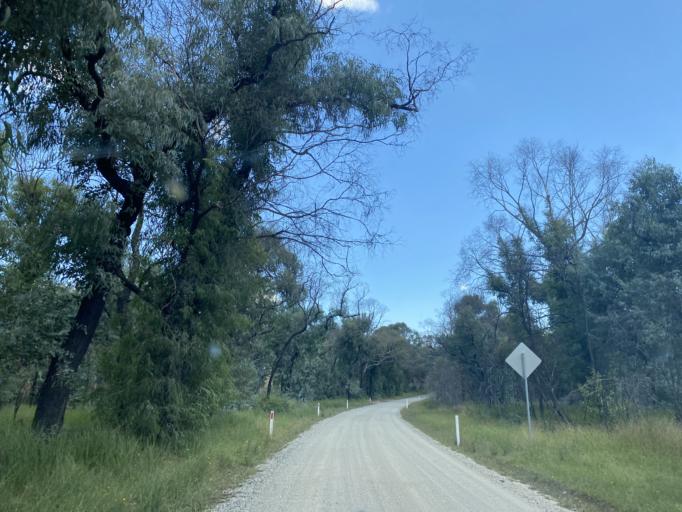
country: AU
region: Victoria
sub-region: Cardinia
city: Garfield
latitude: -37.9910
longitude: 145.6996
